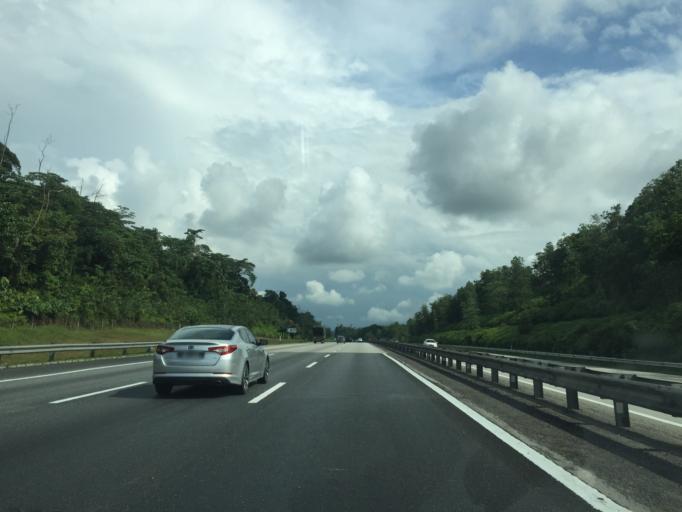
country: MY
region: Selangor
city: Batang Berjuntai
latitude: 3.5598
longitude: 101.5200
